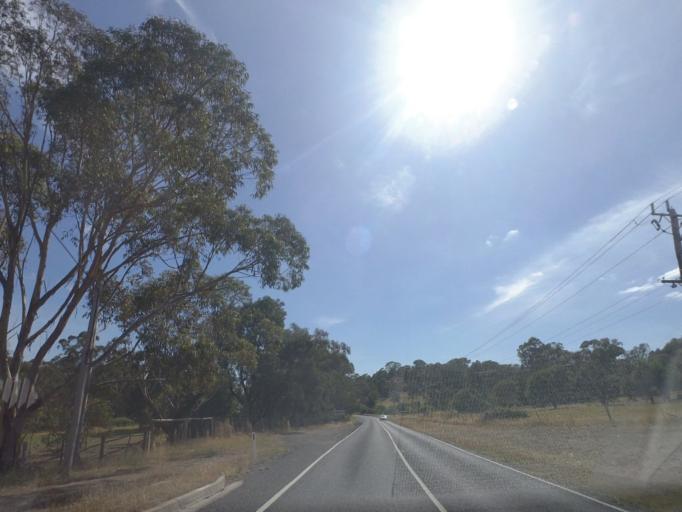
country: AU
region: Victoria
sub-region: Nillumbik
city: Hurstbridge
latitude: -37.6344
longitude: 145.2026
